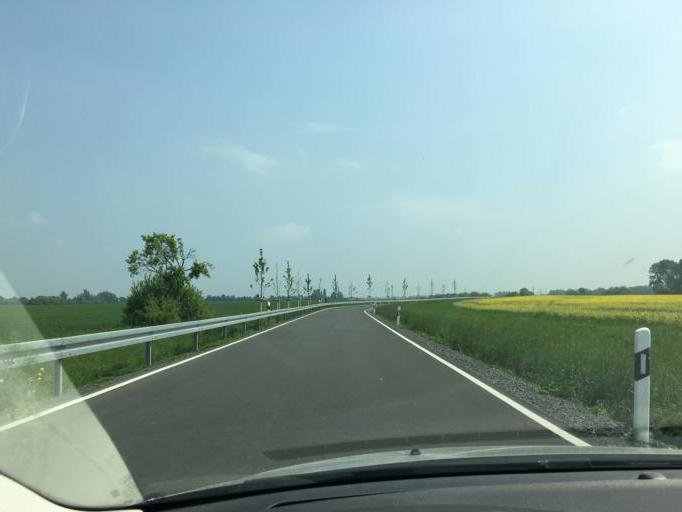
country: DE
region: Saxony
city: Grossposna
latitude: 51.2996
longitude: 12.4818
